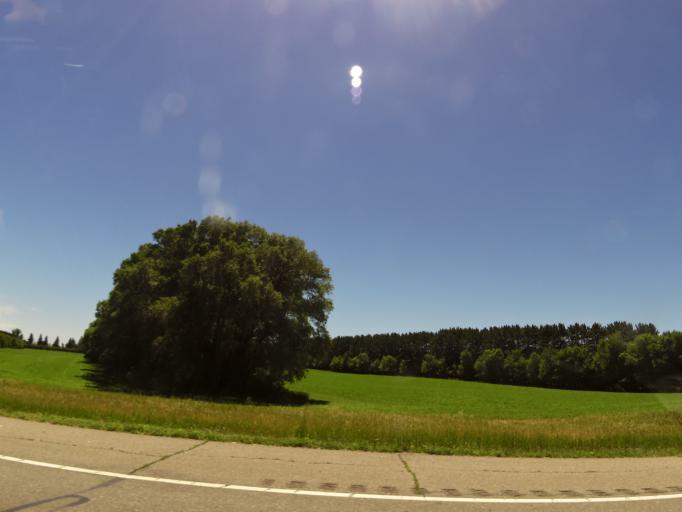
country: US
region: Minnesota
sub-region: Otter Tail County
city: Perham
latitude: 46.5643
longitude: -95.5085
